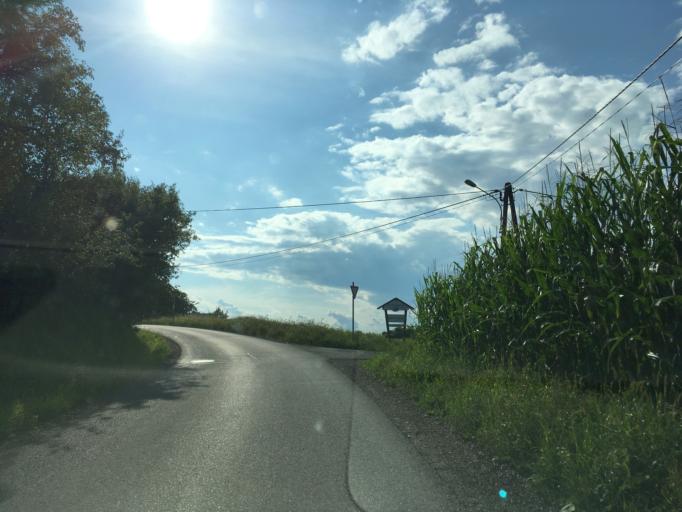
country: AT
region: Styria
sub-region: Politischer Bezirk Leibnitz
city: Sankt Nikolai im Sausal
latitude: 46.8046
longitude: 15.4398
